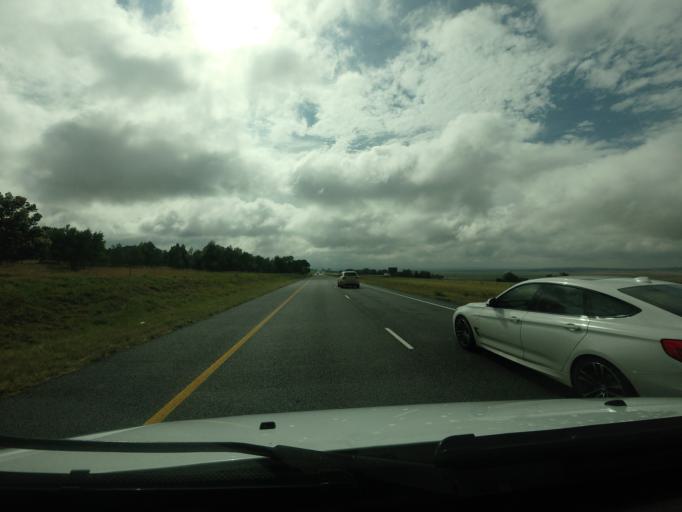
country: ZA
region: Gauteng
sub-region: City of Tshwane Metropolitan Municipality
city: Bronkhorstspruit
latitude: -25.7993
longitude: 28.6320
